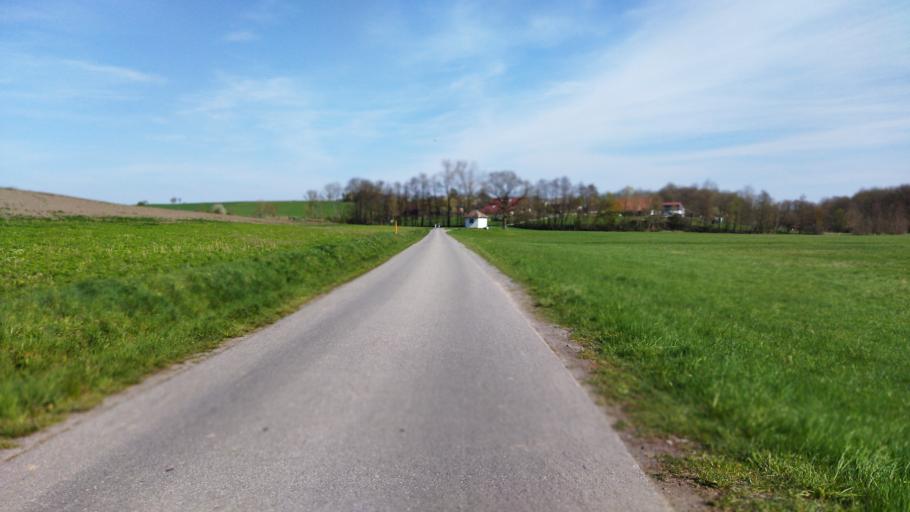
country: DE
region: Baden-Wuerttemberg
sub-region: Regierungsbezirk Stuttgart
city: Sersheim
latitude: 48.9826
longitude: 9.0427
